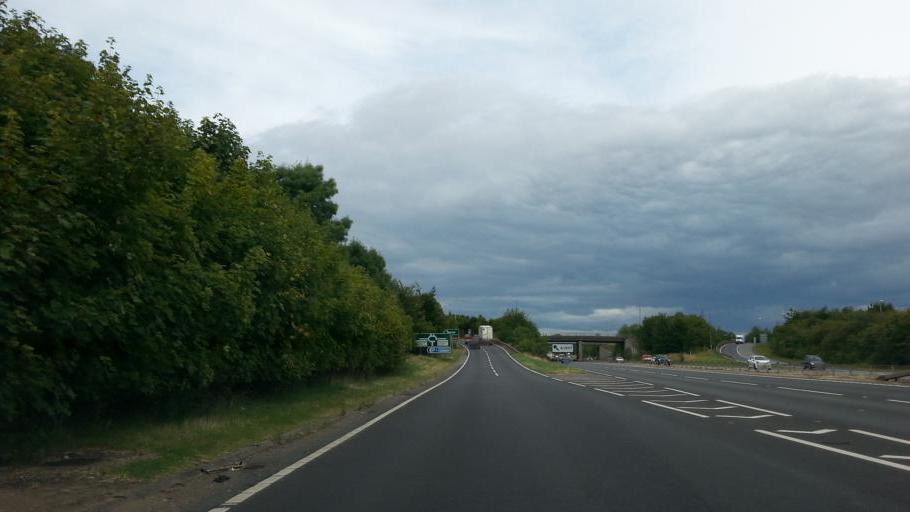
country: GB
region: England
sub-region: Cambridgeshire
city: Sawston
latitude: 52.1271
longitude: 0.2204
